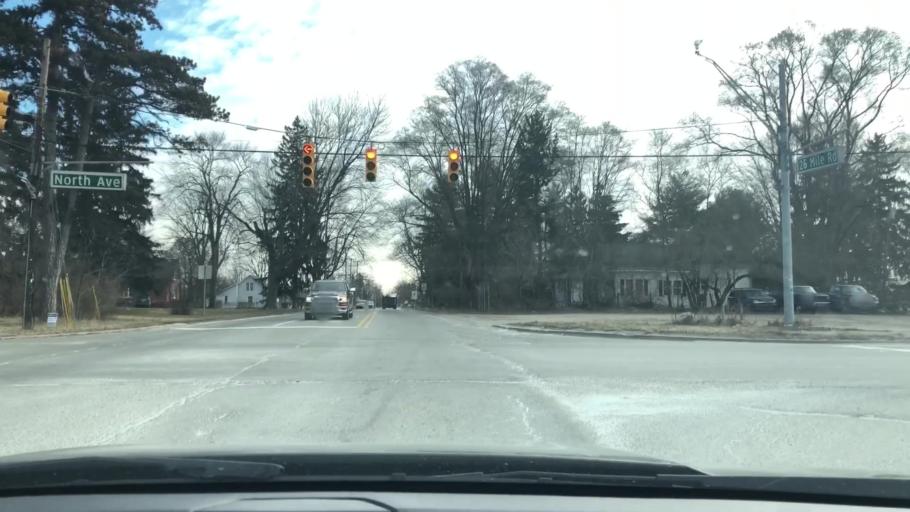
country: US
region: Michigan
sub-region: Macomb County
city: New Haven
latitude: 42.7179
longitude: -82.8749
